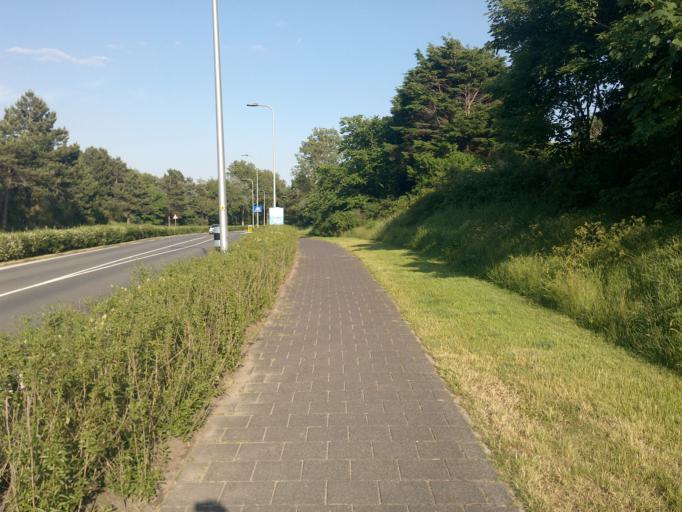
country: NL
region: South Holland
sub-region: Gemeente Noordwijk
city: Noordwijk-Binnen
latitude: 52.2513
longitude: 4.4439
